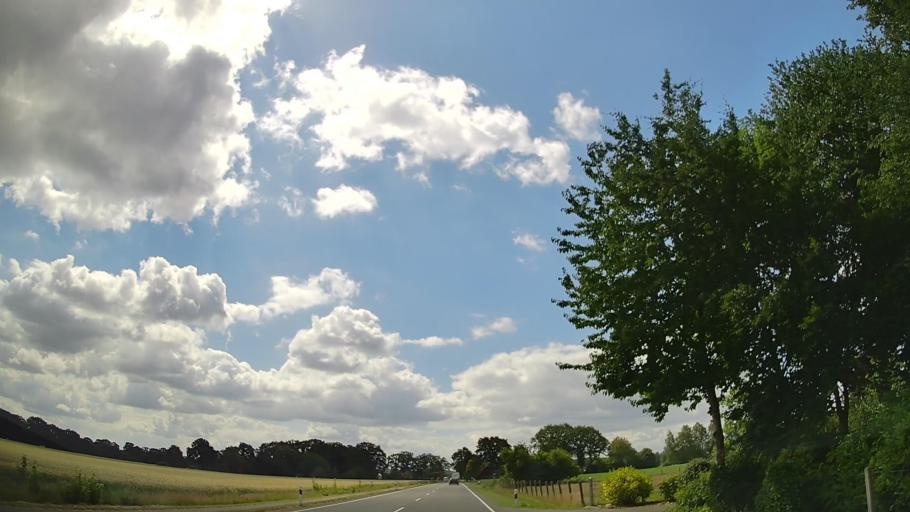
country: DE
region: Lower Saxony
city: Vechta
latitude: 52.6723
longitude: 8.3256
